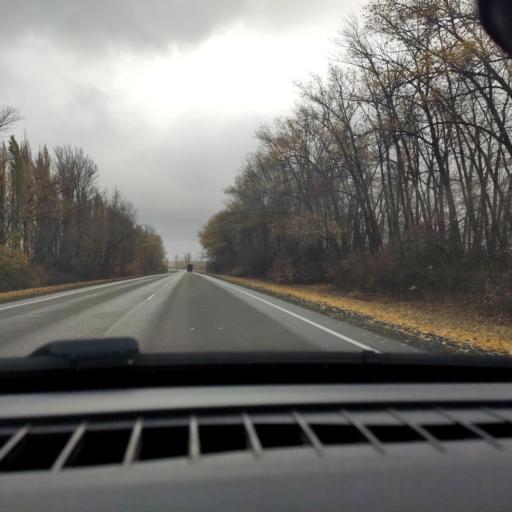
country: RU
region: Voronezj
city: Ostrogozhsk
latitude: 50.9980
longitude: 39.0003
